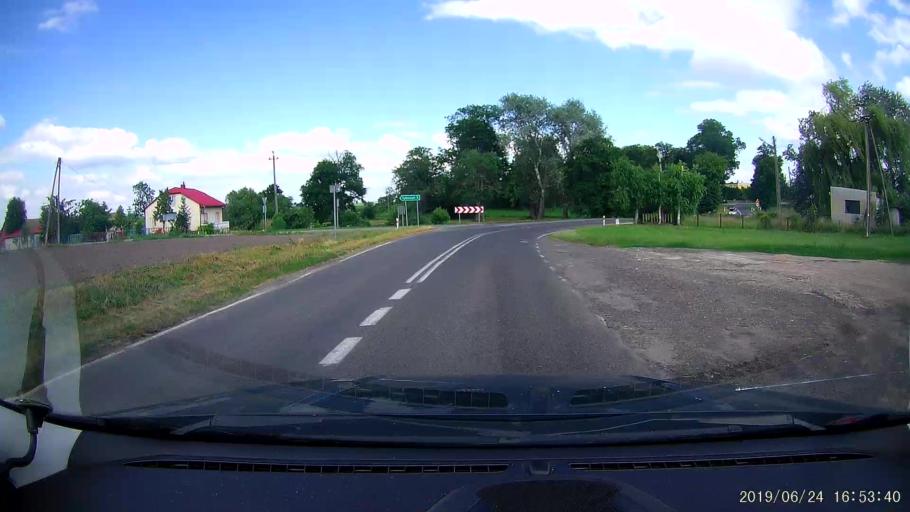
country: PL
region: Lublin Voivodeship
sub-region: Powiat tomaszowski
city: Telatyn
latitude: 50.5351
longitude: 23.8053
